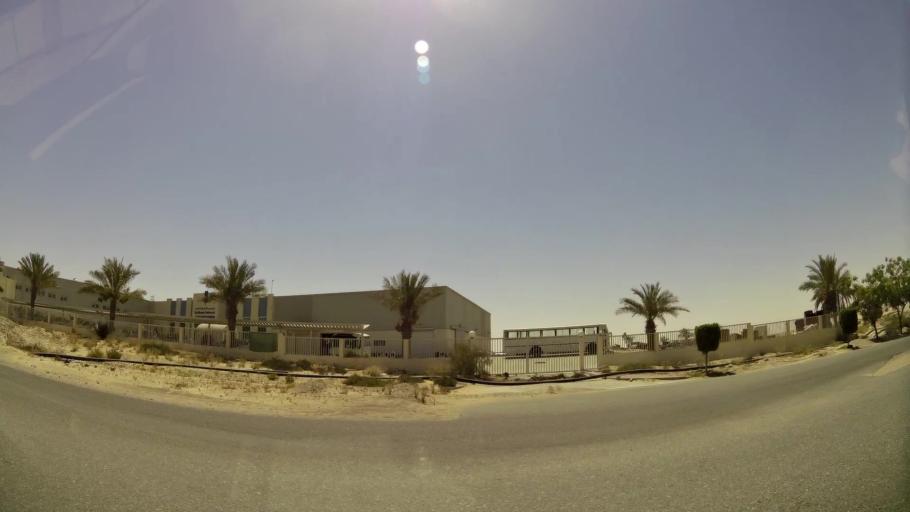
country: AE
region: Dubai
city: Dubai
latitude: 24.9724
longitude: 55.2076
